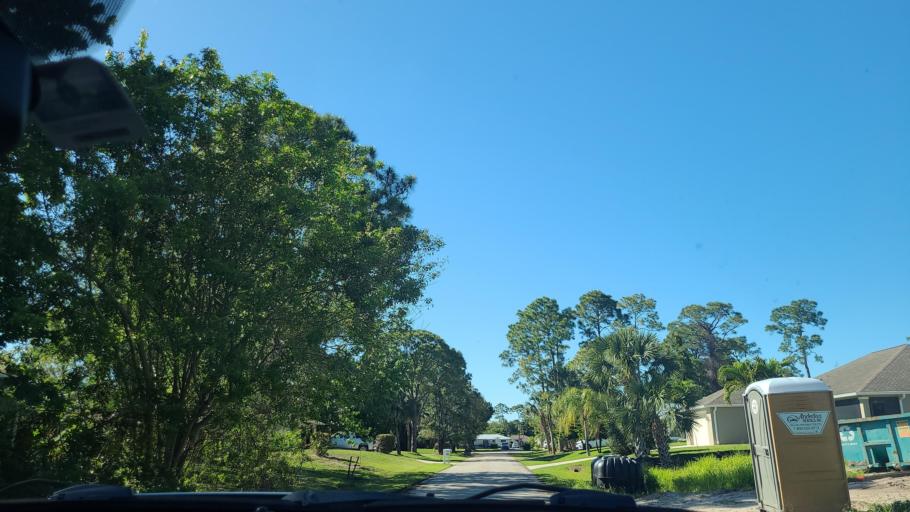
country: US
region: Florida
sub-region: Indian River County
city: Sebastian
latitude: 27.7603
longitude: -80.4764
